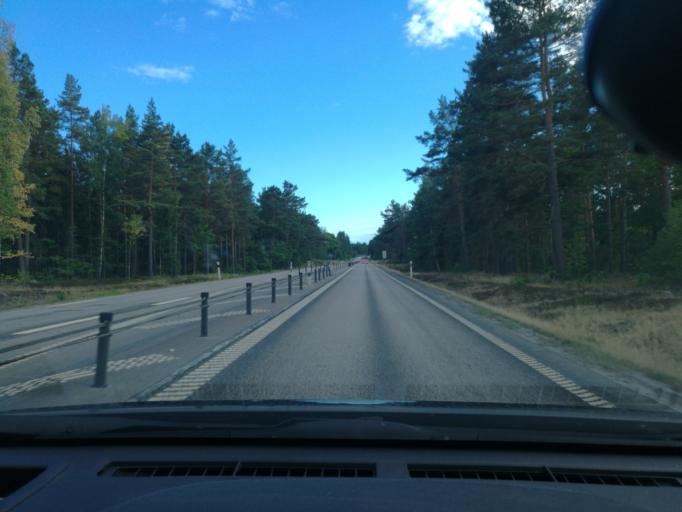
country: SE
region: Kalmar
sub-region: Oskarshamns Kommun
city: Oskarshamn
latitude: 57.3504
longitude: 16.4910
